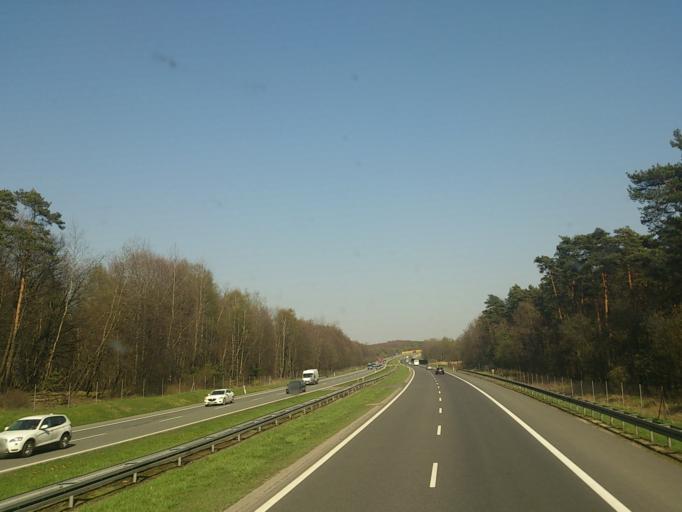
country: PL
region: Lesser Poland Voivodeship
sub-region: Powiat krakowski
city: Zalas
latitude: 50.0904
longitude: 19.6007
